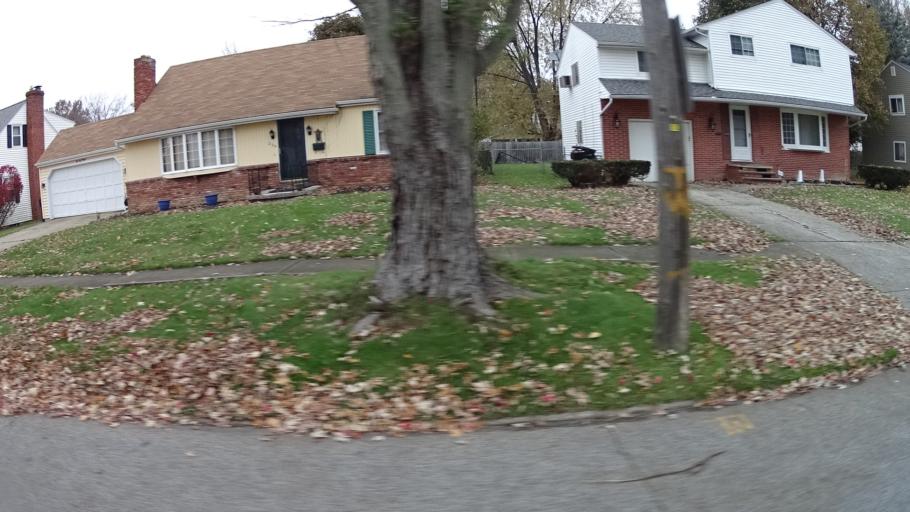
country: US
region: Ohio
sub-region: Lorain County
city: Elyria
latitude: 41.3544
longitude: -82.0964
